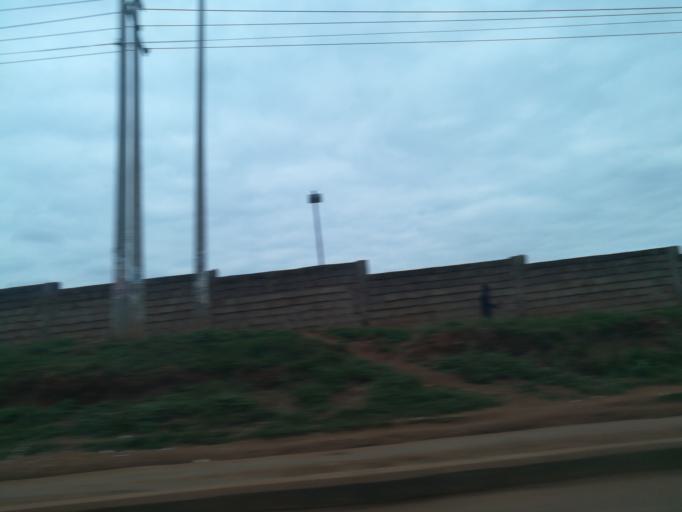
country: KE
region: Nairobi Area
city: Thika
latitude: -1.0677
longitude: 37.0513
